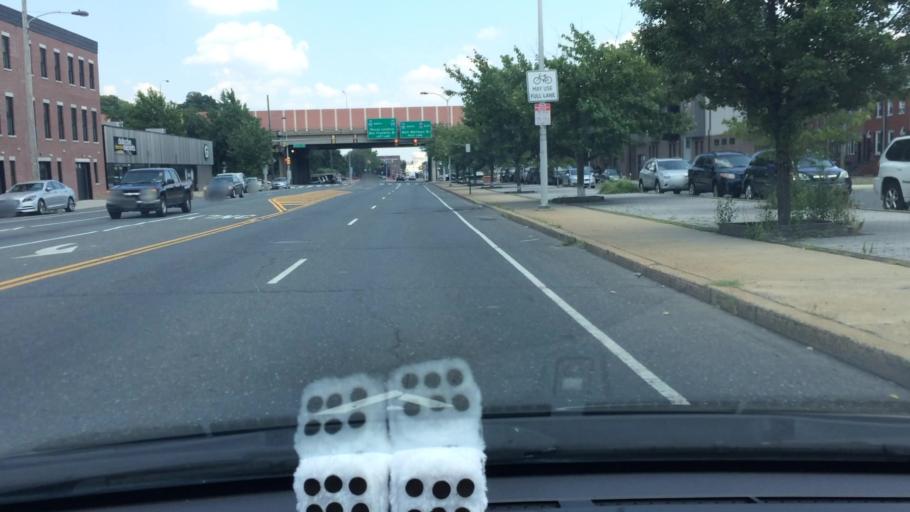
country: US
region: Pennsylvania
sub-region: Philadelphia County
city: Philadelphia
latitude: 39.9338
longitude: -75.1472
